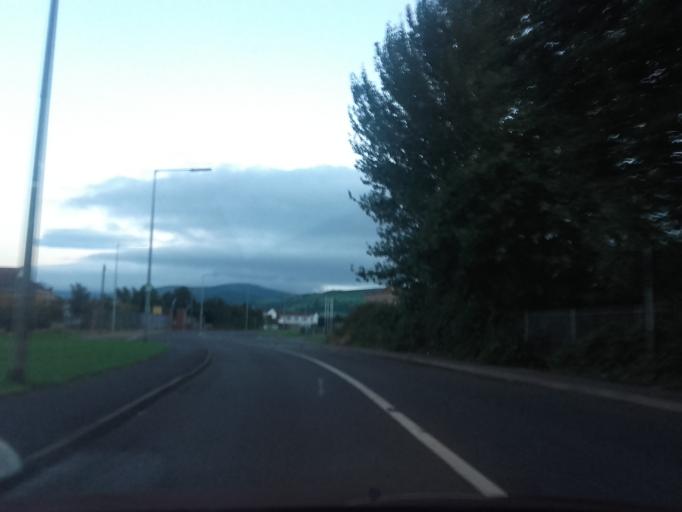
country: IE
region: Leinster
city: Tallaght
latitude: 53.2906
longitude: -6.3878
